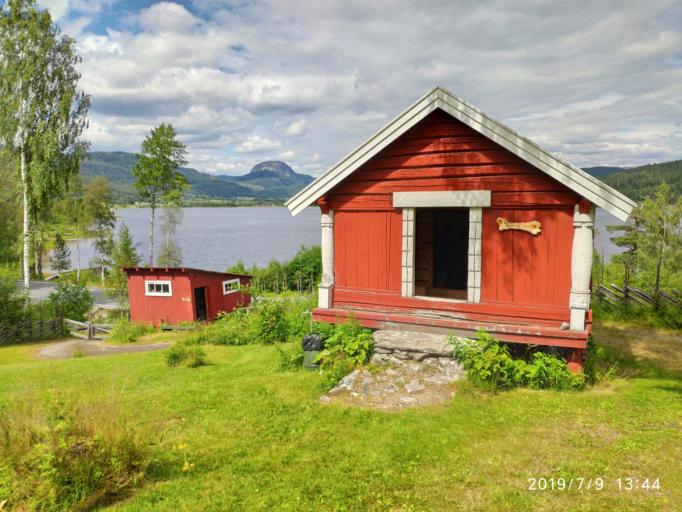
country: NO
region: Buskerud
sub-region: Sigdal
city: Prestfoss
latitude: 60.0619
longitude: 9.5049
